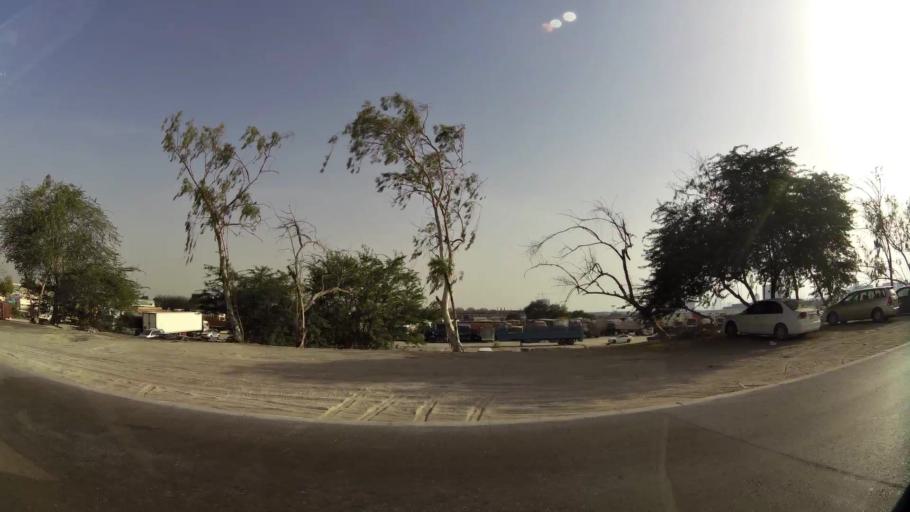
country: AE
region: Ash Shariqah
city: Sharjah
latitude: 25.2351
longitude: 55.3700
